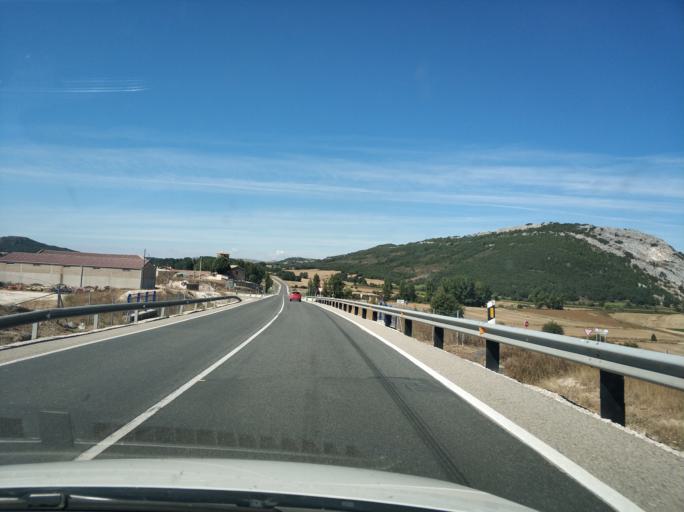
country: ES
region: Castille and Leon
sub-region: Provincia de Burgos
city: Basconcillos del Tozo
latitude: 42.7023
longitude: -3.9873
